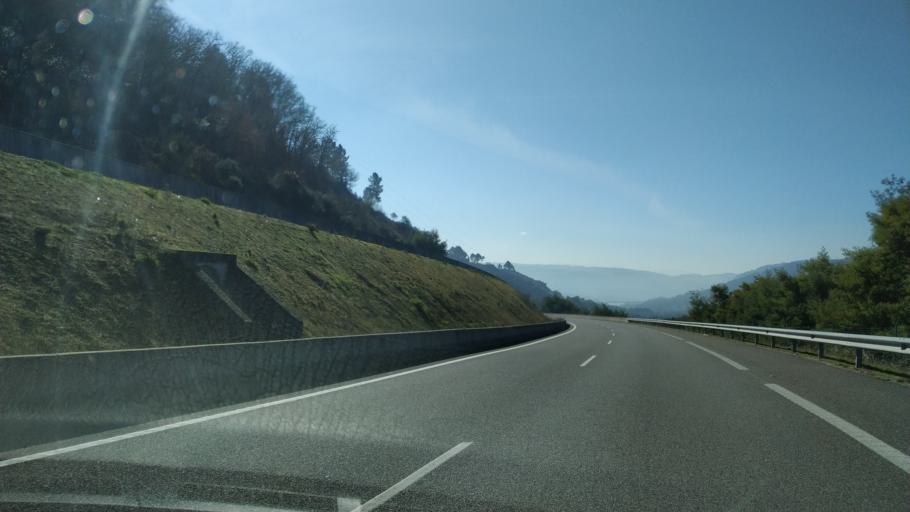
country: ES
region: Galicia
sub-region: Provincia de Ourense
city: Punxin
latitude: 42.3777
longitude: -7.9917
